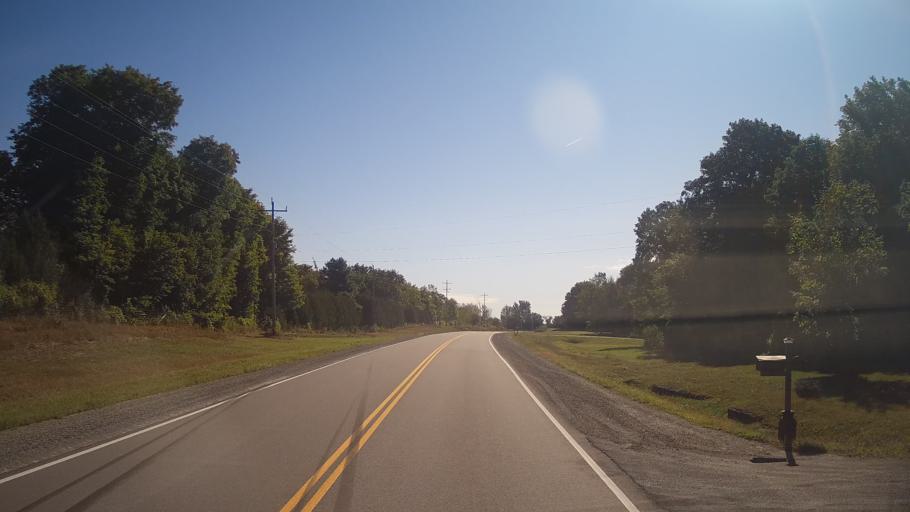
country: CA
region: Ontario
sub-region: Lanark County
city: Smiths Falls
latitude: 44.6254
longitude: -75.9848
